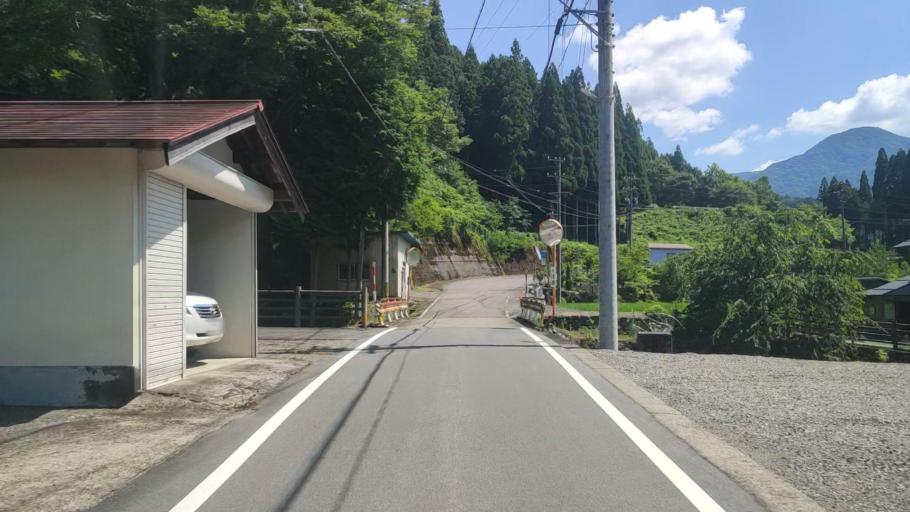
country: JP
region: Gifu
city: Godo
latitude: 35.6692
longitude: 136.5780
